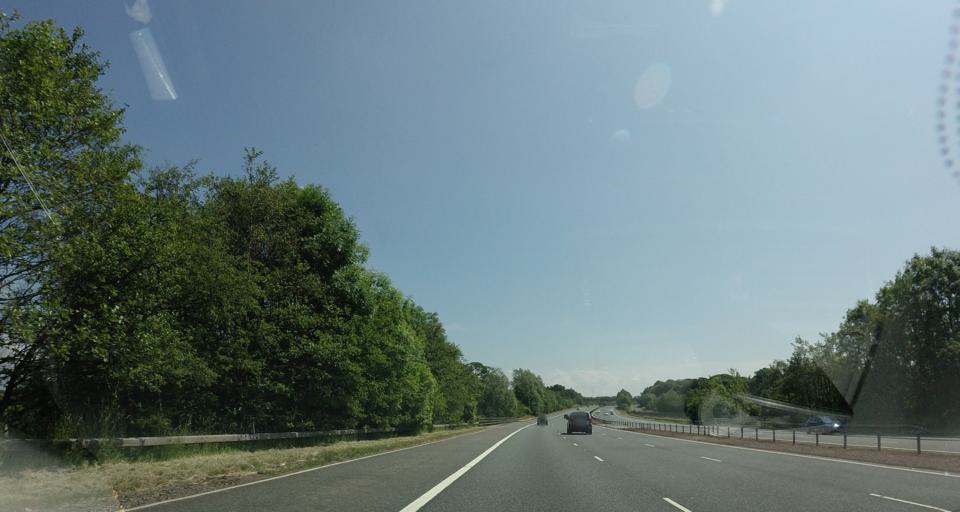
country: GB
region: Scotland
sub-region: Dumfries and Galloway
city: Annan
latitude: 55.0461
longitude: -3.1926
